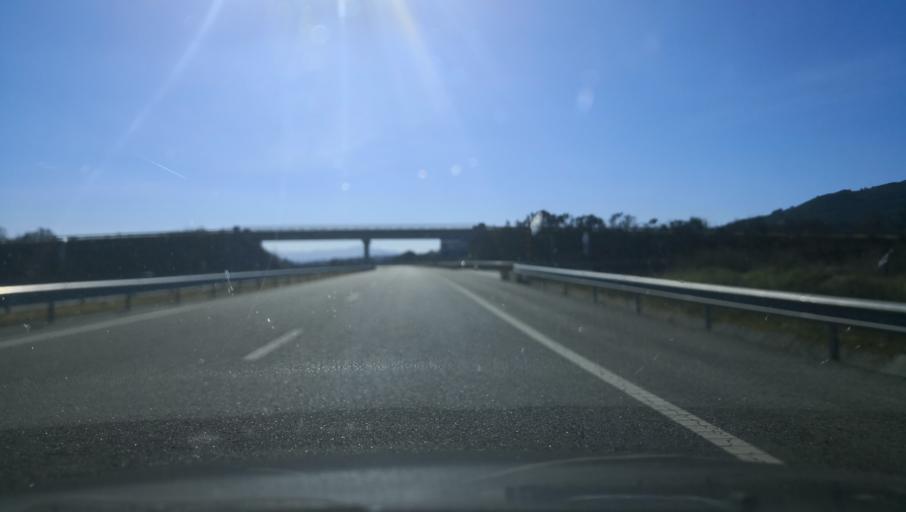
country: PT
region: Vila Real
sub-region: Chaves
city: Chaves
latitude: 41.7508
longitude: -7.5200
